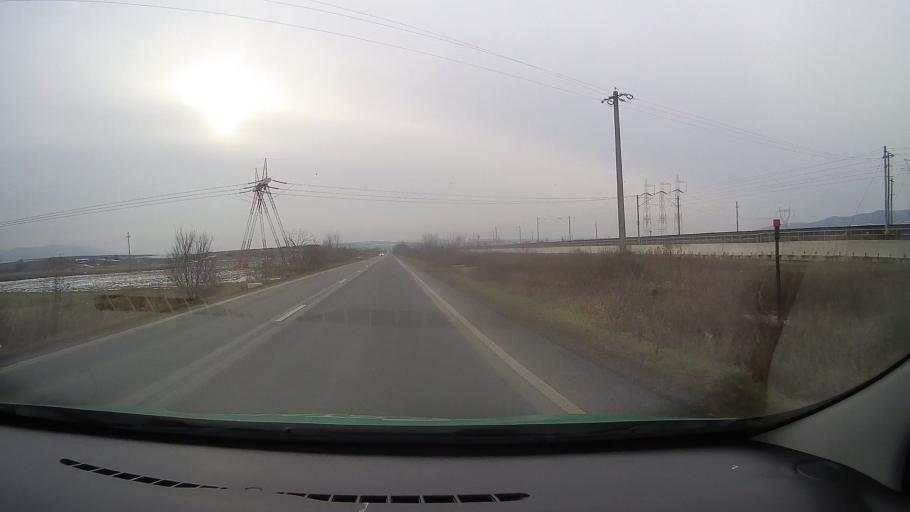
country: RO
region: Hunedoara
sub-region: Comuna Geoagiu
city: Geoagiu
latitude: 45.8755
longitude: 23.2371
